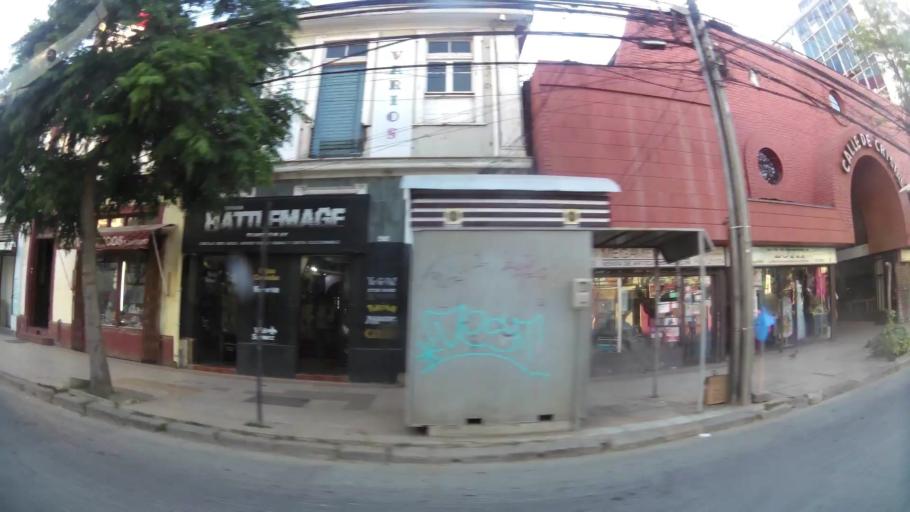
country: CL
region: Valparaiso
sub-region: Provincia de Valparaiso
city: Vina del Mar
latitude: -33.0235
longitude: -71.5559
